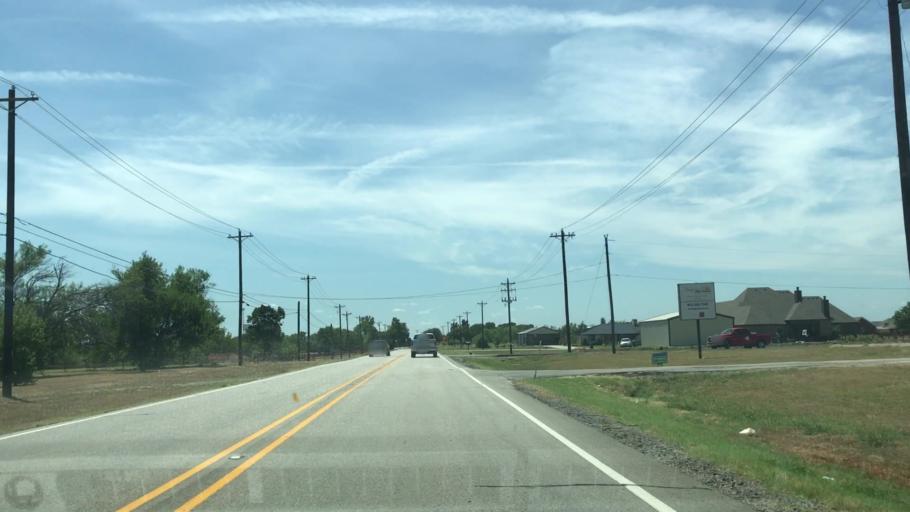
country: US
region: Texas
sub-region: Collin County
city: Saint Paul
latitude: 33.0409
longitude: -96.5503
